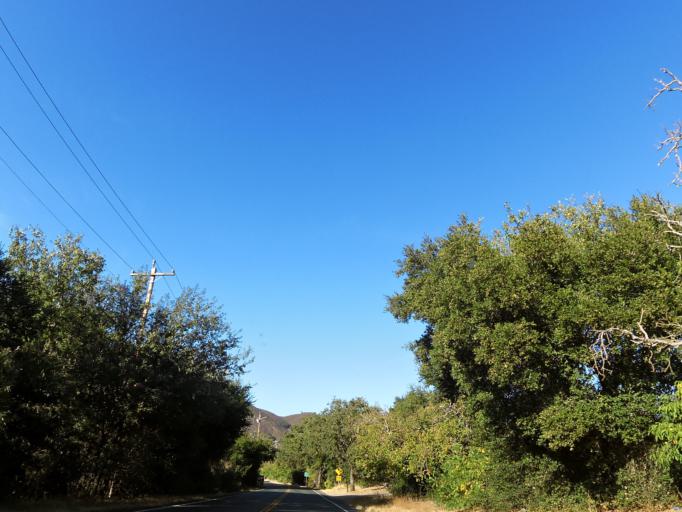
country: US
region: California
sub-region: Santa Clara County
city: San Martin
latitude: 37.0436
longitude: -121.6541
